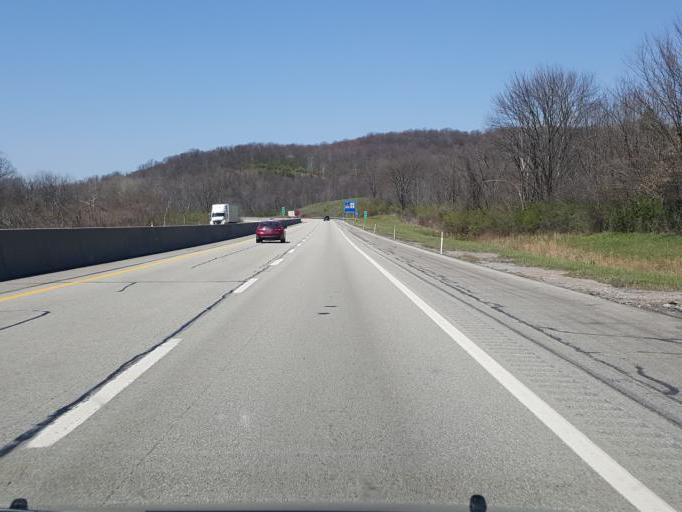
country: US
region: Pennsylvania
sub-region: Westmoreland County
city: Youngwood
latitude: 40.2103
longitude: -79.5778
